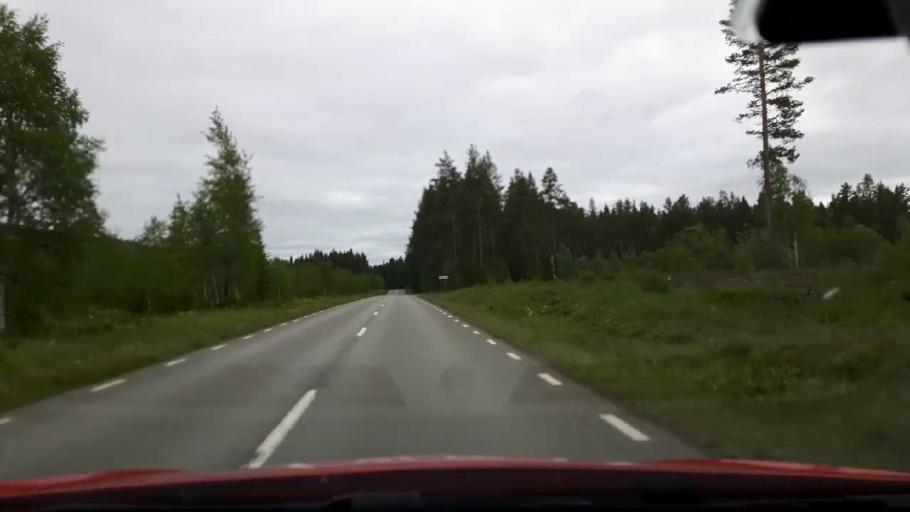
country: SE
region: Jaemtland
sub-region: Stroemsunds Kommun
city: Stroemsund
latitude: 63.4375
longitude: 15.4882
